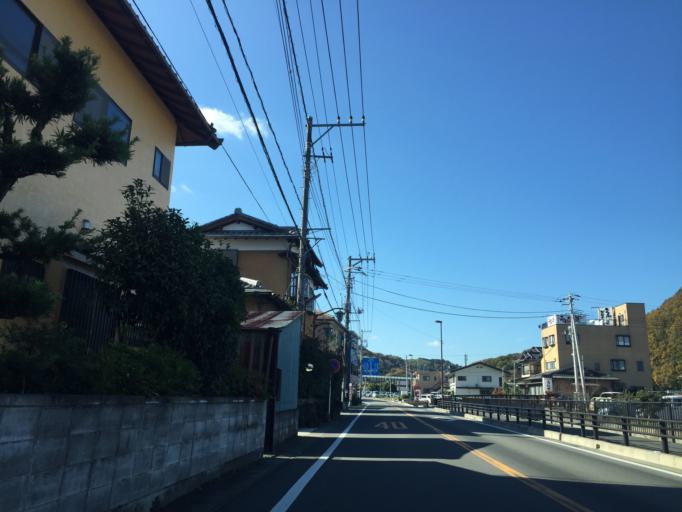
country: JP
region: Shizuoka
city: Mishima
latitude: 35.0273
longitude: 138.9285
